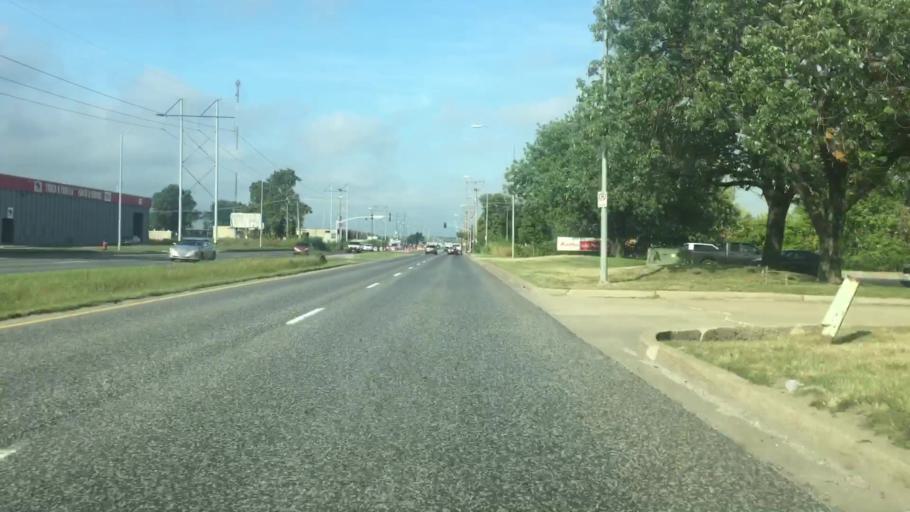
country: US
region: Missouri
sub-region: Clay County
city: North Kansas City
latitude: 39.1305
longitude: -94.5119
